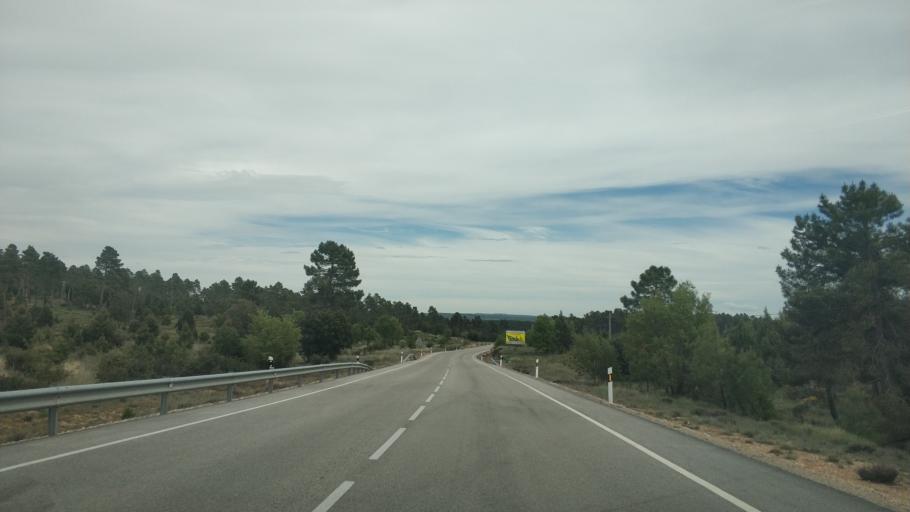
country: ES
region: Castille and Leon
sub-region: Provincia de Soria
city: Quintanas de Gormaz
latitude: 41.5239
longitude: -2.9398
